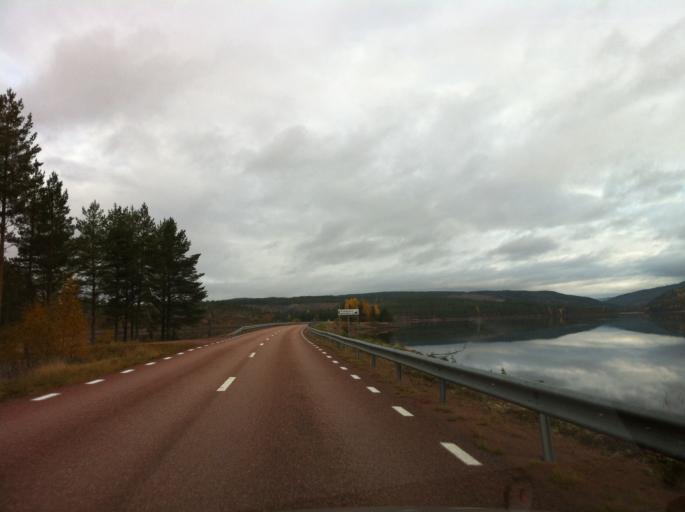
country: SE
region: Dalarna
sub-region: Alvdalens Kommun
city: AElvdalen
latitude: 61.2967
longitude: 13.7312
